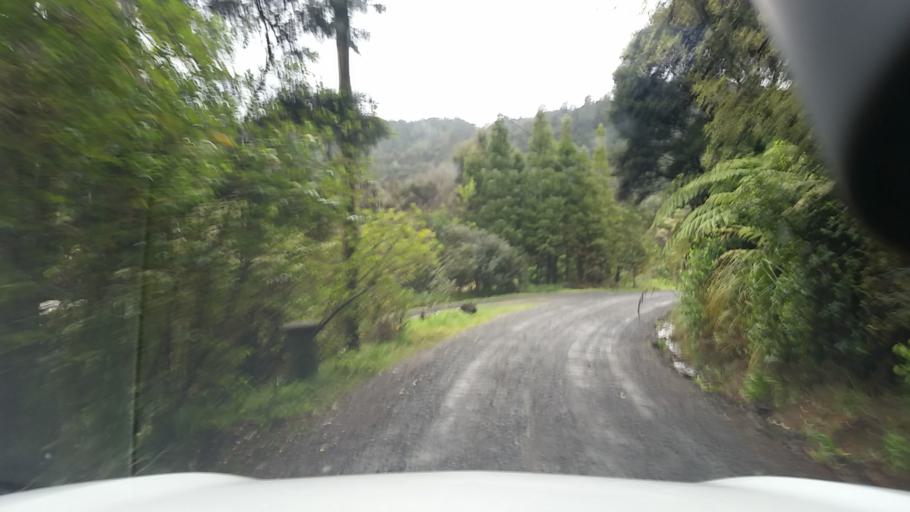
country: NZ
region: Auckland
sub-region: Auckland
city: Waitakere
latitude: -36.9010
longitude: 174.5712
